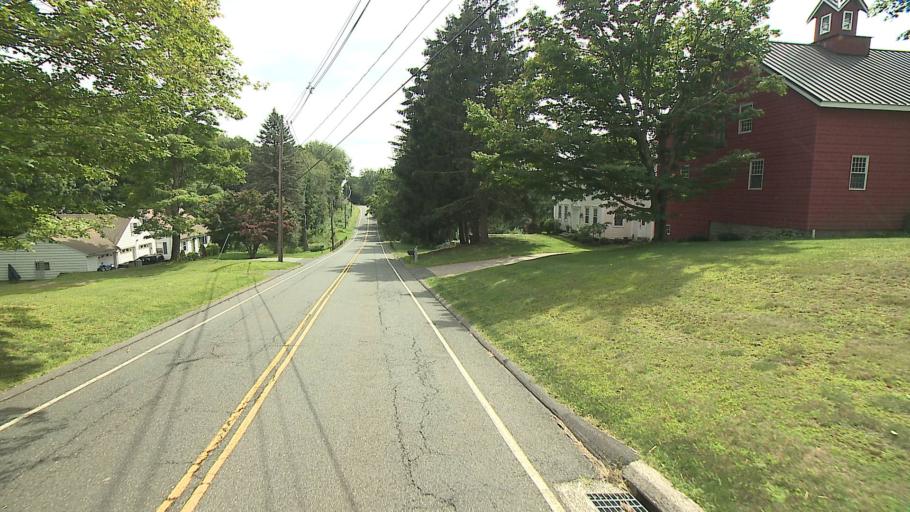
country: US
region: Connecticut
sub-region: Litchfield County
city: Bethlehem Village
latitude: 41.6080
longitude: -73.2434
